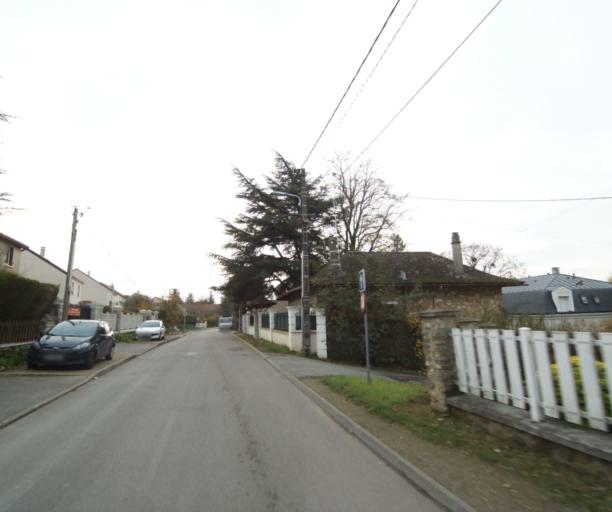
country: FR
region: Ile-de-France
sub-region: Departement des Yvelines
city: Triel-sur-Seine
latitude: 48.9884
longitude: 1.9992
